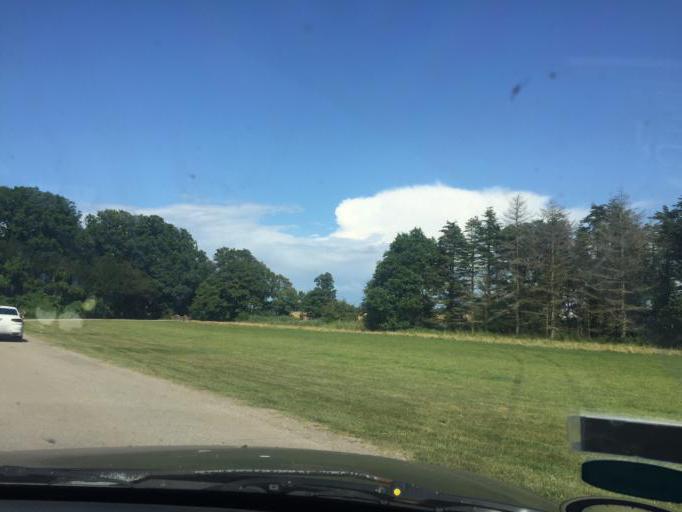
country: DK
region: Zealand
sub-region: Lolland Kommune
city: Maribo
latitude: 54.8219
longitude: 11.5155
